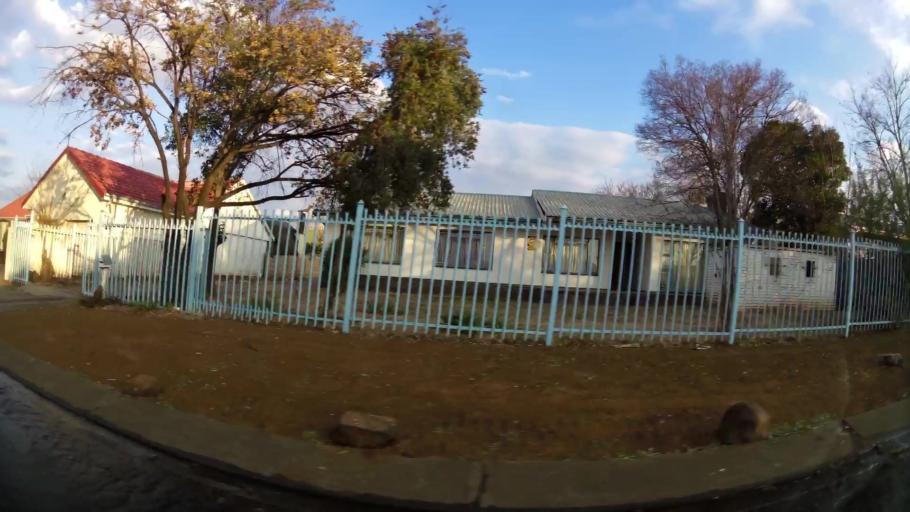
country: ZA
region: Orange Free State
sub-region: Mangaung Metropolitan Municipality
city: Bloemfontein
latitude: -29.1419
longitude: 26.1819
